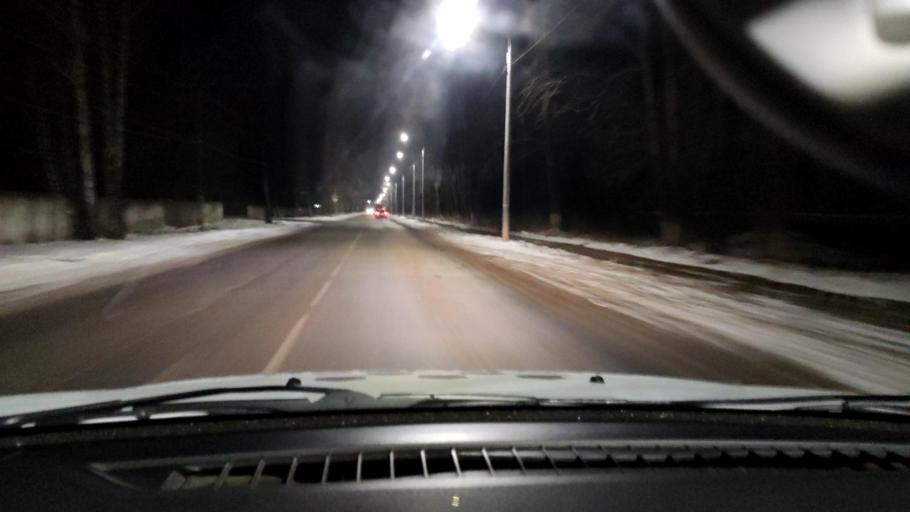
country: RU
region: Perm
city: Kultayevo
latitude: 57.9809
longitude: 55.9175
